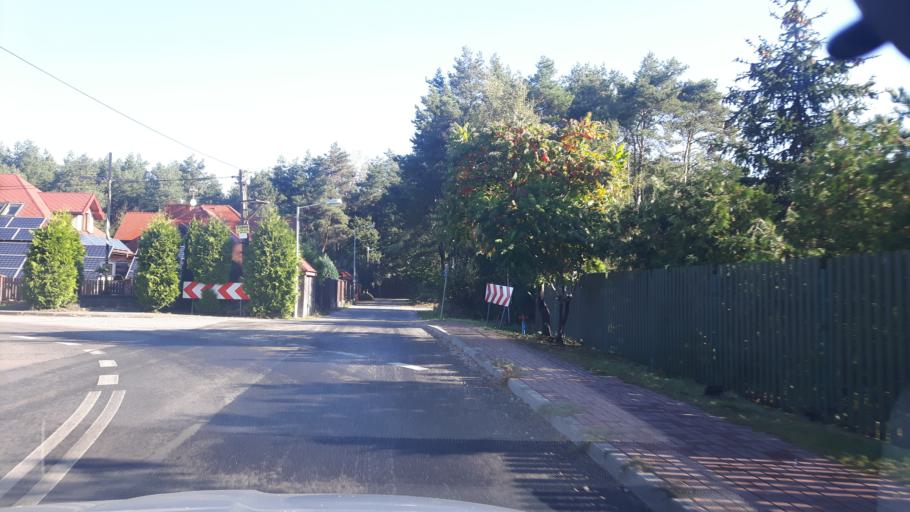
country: PL
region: Masovian Voivodeship
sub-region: Powiat legionowski
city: Michalow-Reginow
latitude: 52.4014
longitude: 20.9940
